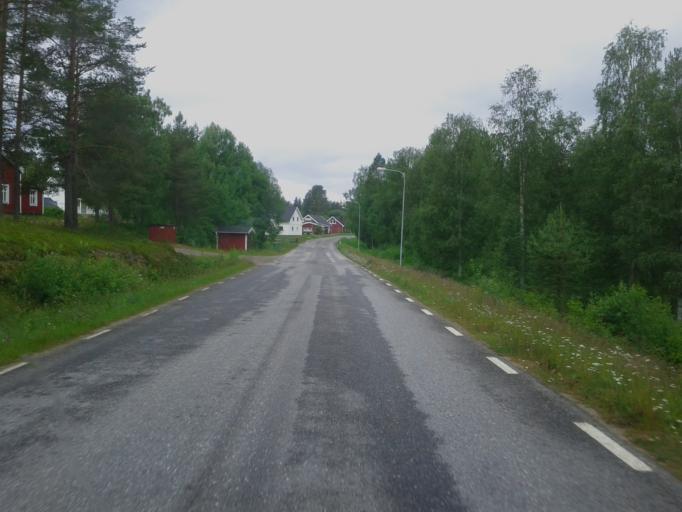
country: SE
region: Vaesterbotten
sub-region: Skelleftea Kommun
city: Kage
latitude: 64.9143
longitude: 20.9667
